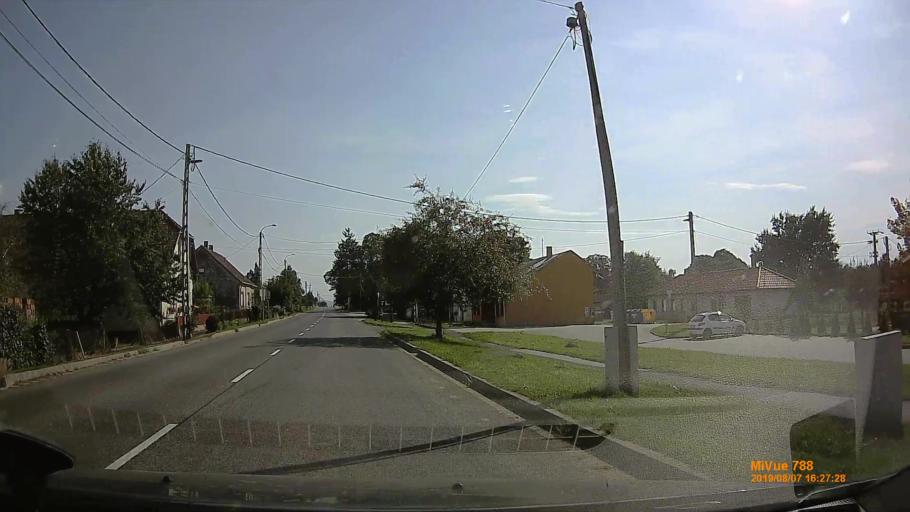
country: HU
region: Zala
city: Lenti
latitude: 46.7021
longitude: 16.5493
